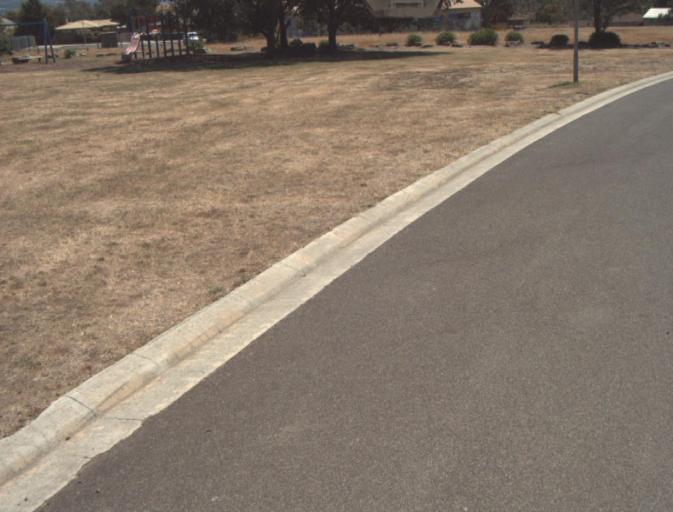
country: AU
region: Tasmania
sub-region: Launceston
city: Mayfield
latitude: -41.3755
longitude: 147.1396
